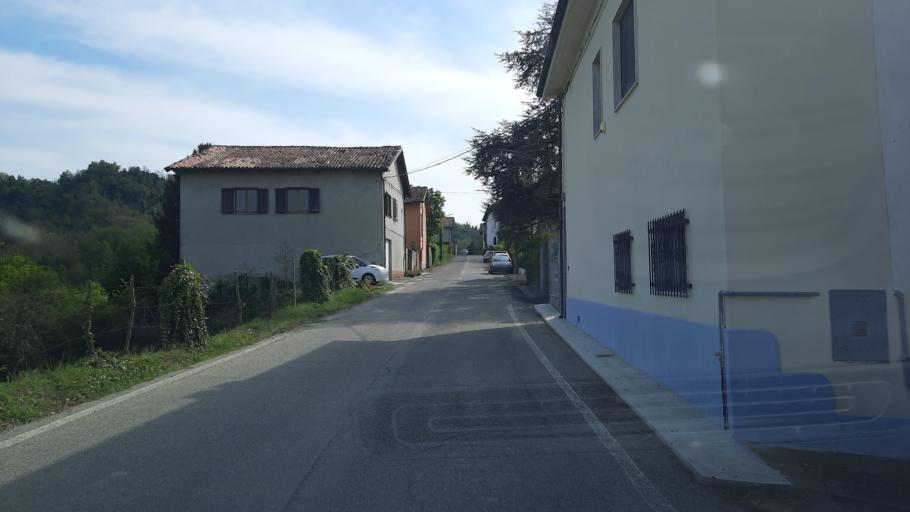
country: IT
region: Piedmont
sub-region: Provincia di Alessandria
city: Camino
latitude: 45.1691
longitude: 8.2637
